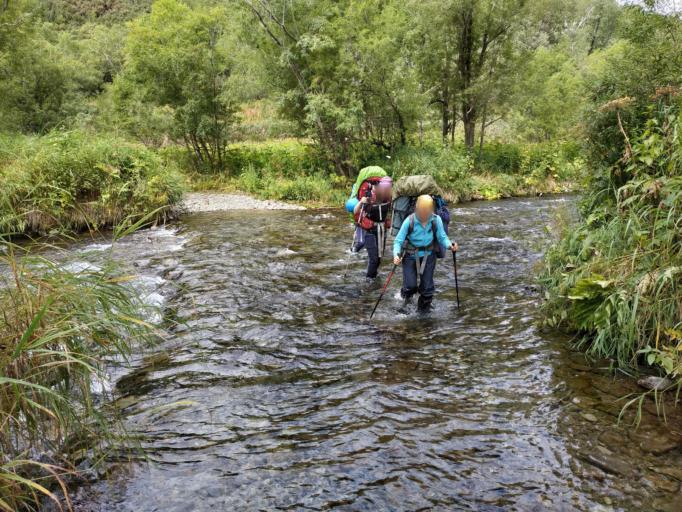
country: RU
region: Kamtsjatka
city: Yelizovo
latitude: 53.7868
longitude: 158.1416
